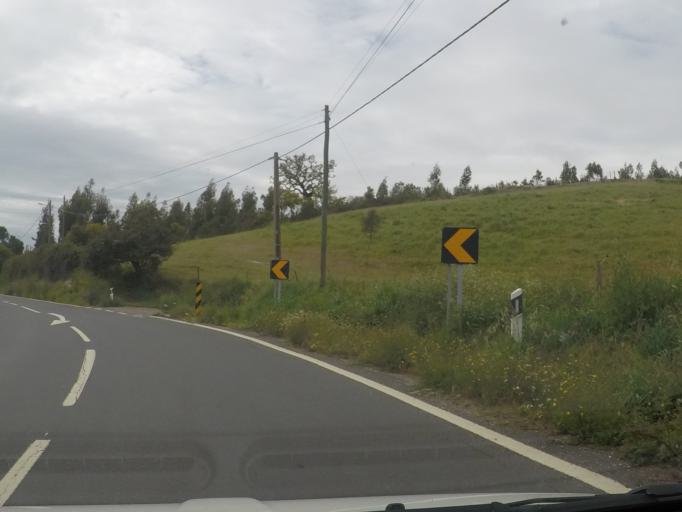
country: PT
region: Setubal
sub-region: Sines
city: Porto Covo
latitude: 37.8681
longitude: -8.7366
